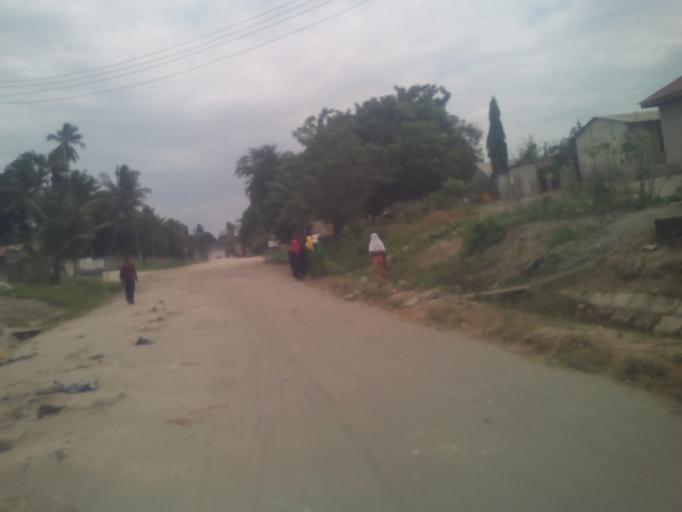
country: TZ
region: Dar es Salaam
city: Dar es Salaam
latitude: -6.8723
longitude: 39.2279
